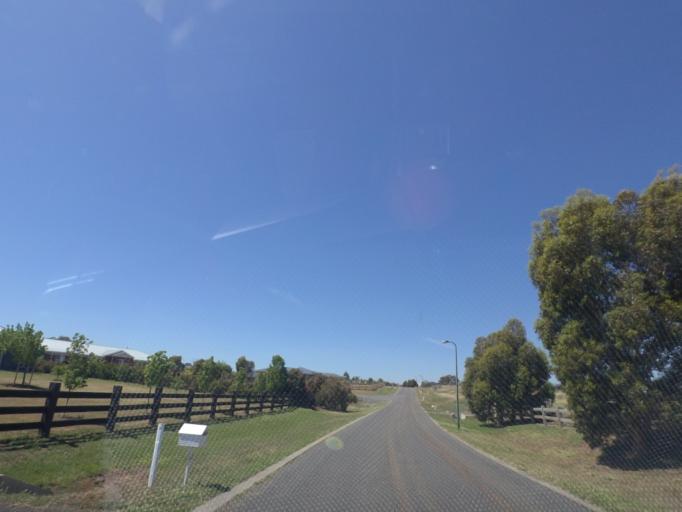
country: AU
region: Victoria
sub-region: Melton
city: Brookfield
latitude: -37.7031
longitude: 144.5092
